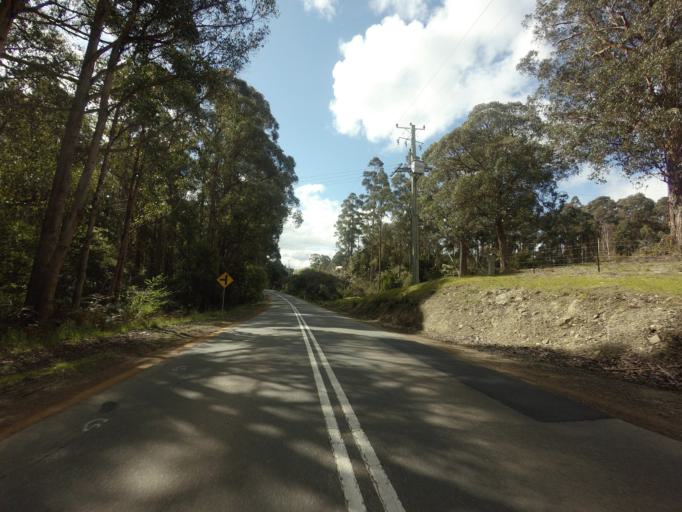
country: AU
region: Tasmania
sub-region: Huon Valley
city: Geeveston
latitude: -43.2239
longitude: 146.9880
